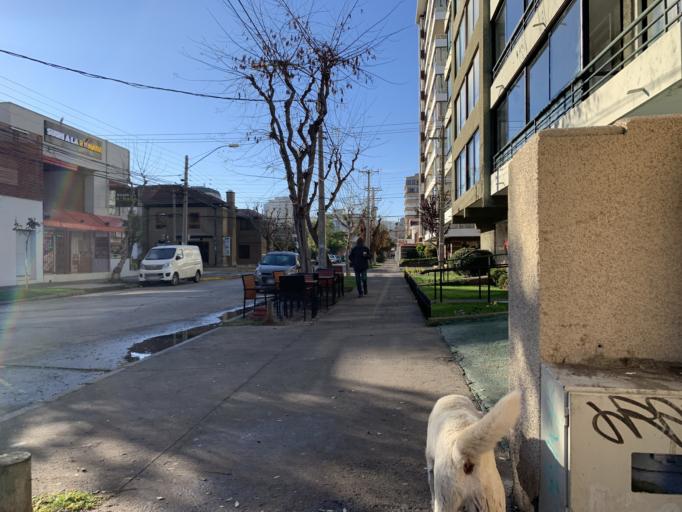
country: CL
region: Valparaiso
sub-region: Provincia de Valparaiso
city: Vina del Mar
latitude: -33.0175
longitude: -71.5573
